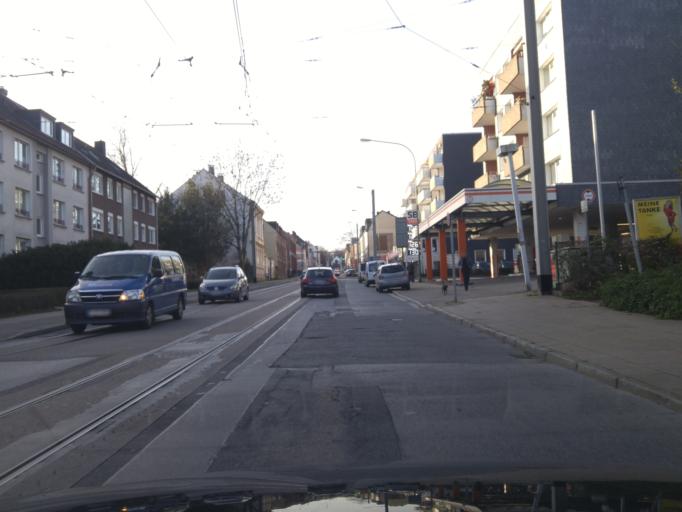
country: DE
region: North Rhine-Westphalia
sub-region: Regierungsbezirk Dusseldorf
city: Essen
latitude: 51.4272
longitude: 7.0474
